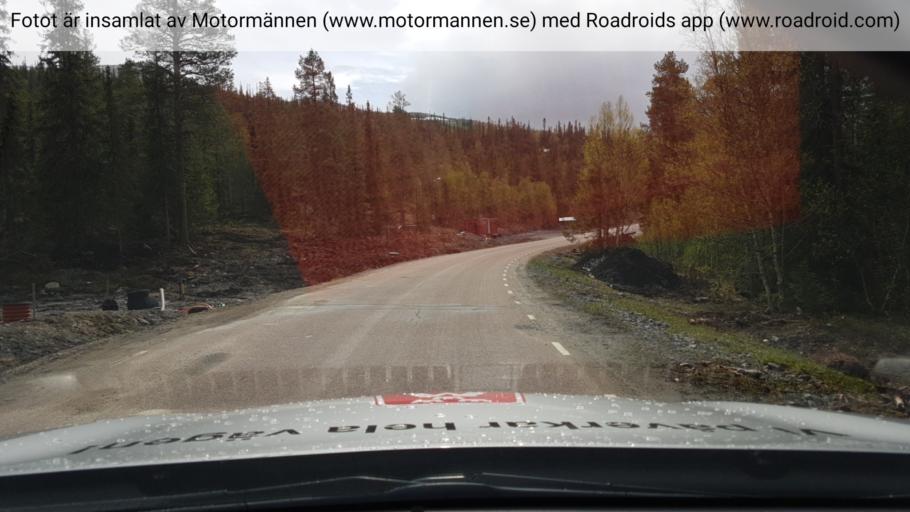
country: SE
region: Jaemtland
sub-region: Are Kommun
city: Jarpen
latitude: 63.0819
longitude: 13.7721
